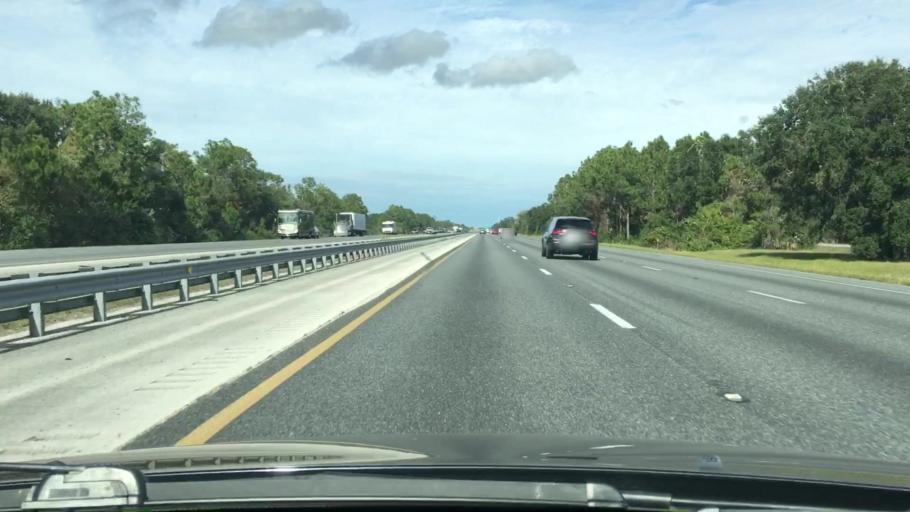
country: US
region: Florida
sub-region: Volusia County
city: Ormond-by-the-Sea
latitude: 29.3076
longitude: -81.1317
